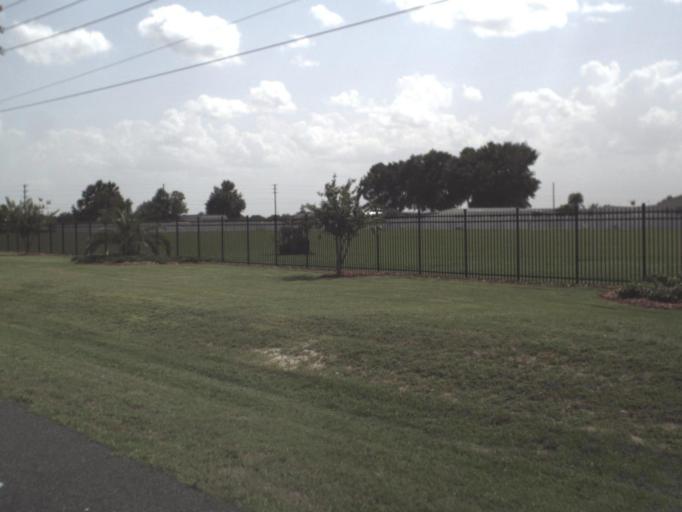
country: US
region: Florida
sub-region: Polk County
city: Lake Hamilton
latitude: 28.0668
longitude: -81.6417
